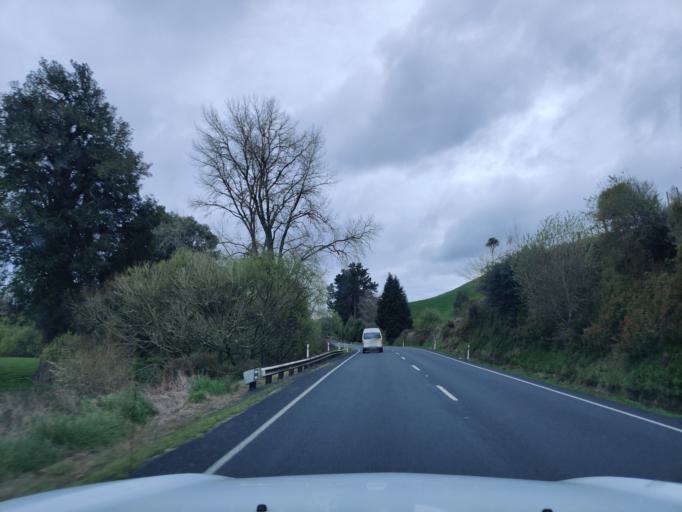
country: NZ
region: Waikato
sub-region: Otorohanga District
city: Otorohanga
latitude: -38.4766
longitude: 175.1741
